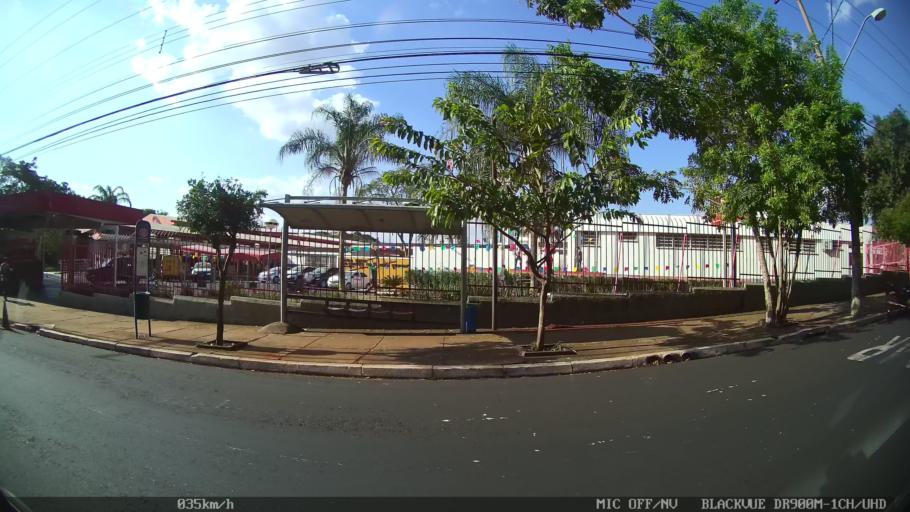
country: BR
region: Sao Paulo
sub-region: Ribeirao Preto
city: Ribeirao Preto
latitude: -21.1709
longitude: -47.8000
